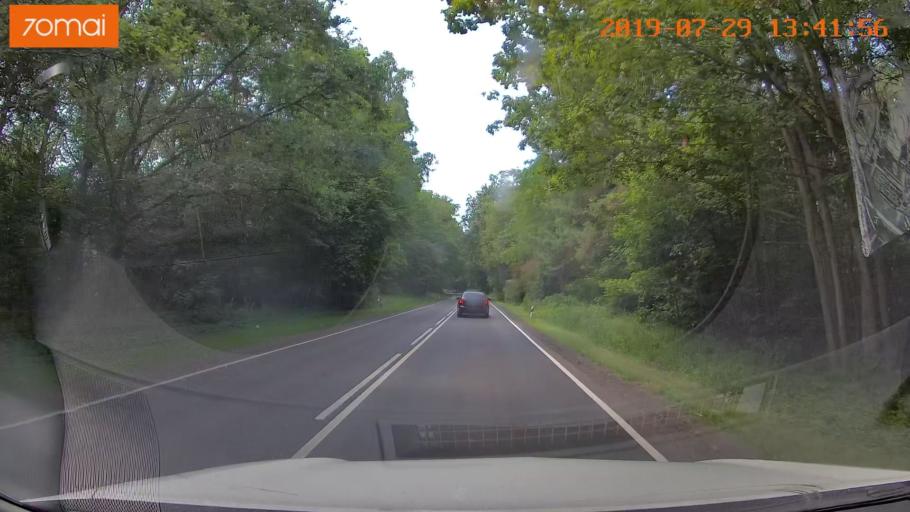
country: RU
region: Kaliningrad
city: Svetlyy
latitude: 54.7362
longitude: 20.1200
